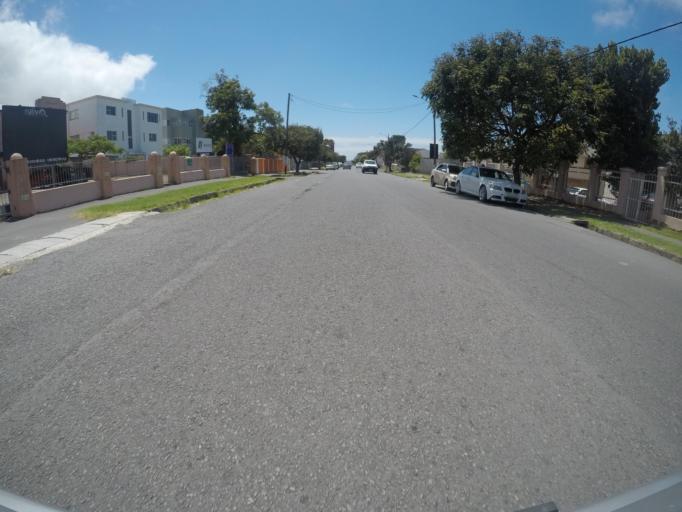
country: ZA
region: Eastern Cape
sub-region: Buffalo City Metropolitan Municipality
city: East London
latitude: -33.0004
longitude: 27.9027
